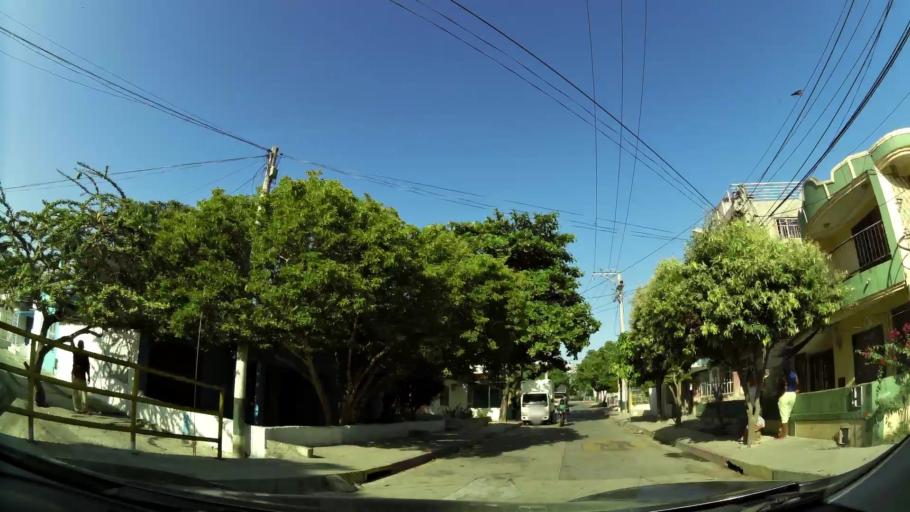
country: CO
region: Bolivar
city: Cartagena
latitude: 10.4031
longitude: -75.4992
